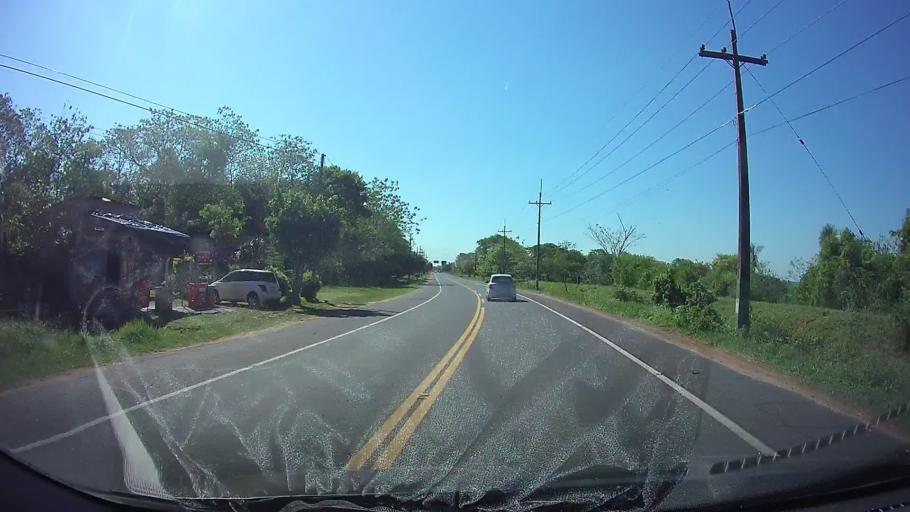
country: PY
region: Central
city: Ypacarai
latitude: -25.3932
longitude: -57.2939
